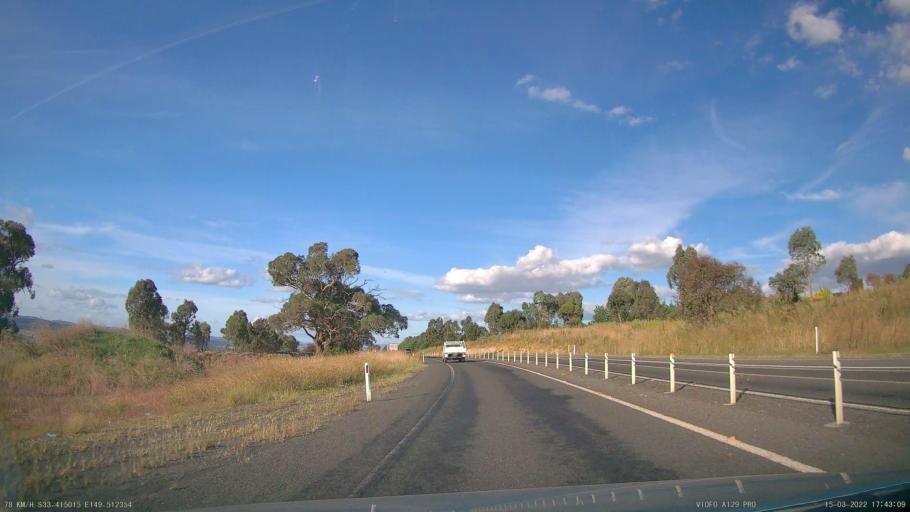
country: AU
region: New South Wales
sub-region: Bathurst Regional
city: Eglinton
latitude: -33.4149
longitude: 149.5126
